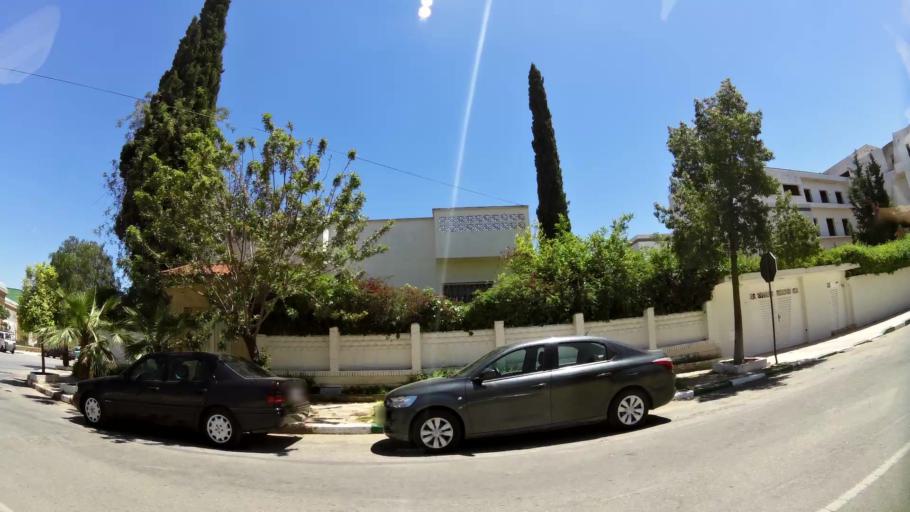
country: MA
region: Meknes-Tafilalet
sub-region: Meknes
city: Meknes
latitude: 33.9055
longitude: -5.5601
